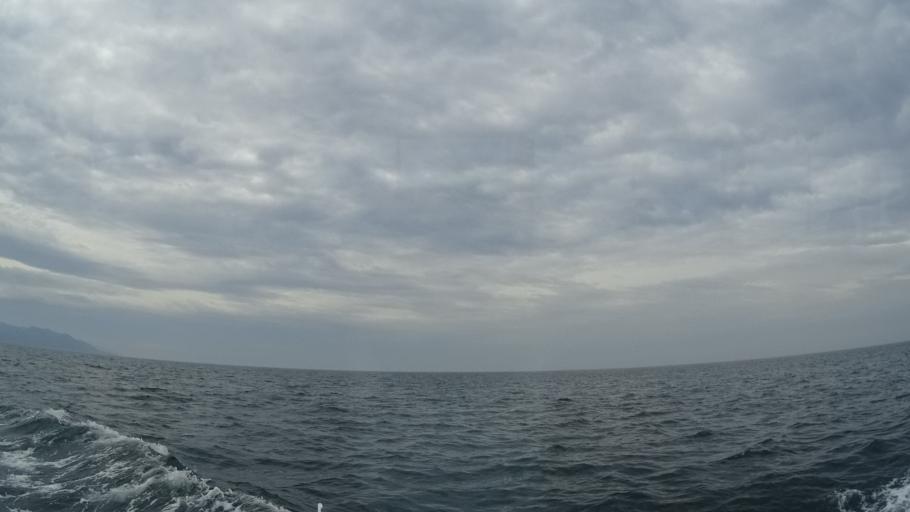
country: JP
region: Fukui
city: Mikuni
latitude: 36.2460
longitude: 136.1198
